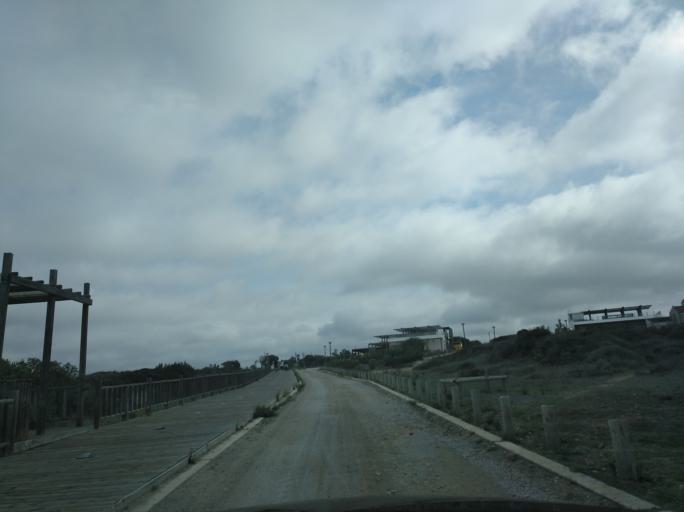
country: PT
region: Setubal
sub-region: Santiago do Cacem
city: Santo Andre
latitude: 38.1289
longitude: -8.7905
